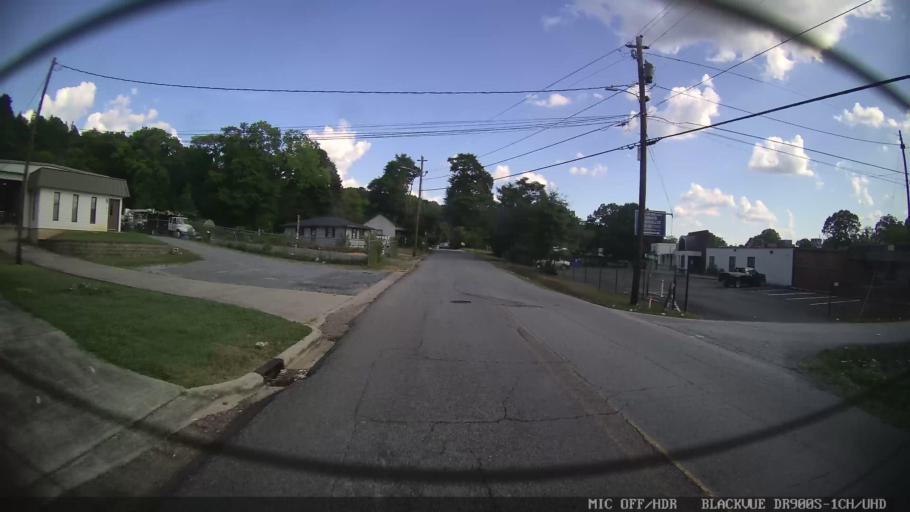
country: US
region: Georgia
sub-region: Floyd County
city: Rome
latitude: 34.2352
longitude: -85.1586
